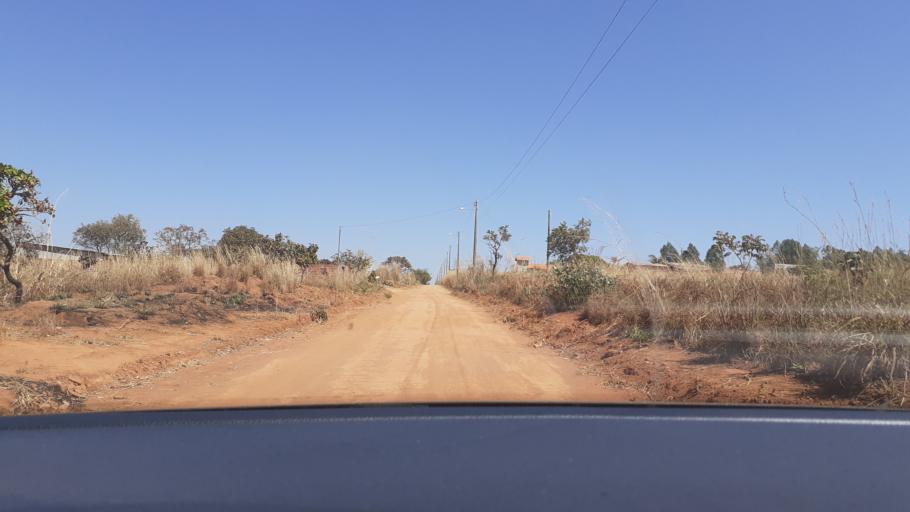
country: BR
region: Goias
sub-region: Aparecida De Goiania
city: Aparecida de Goiania
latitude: -16.8706
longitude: -49.2733
